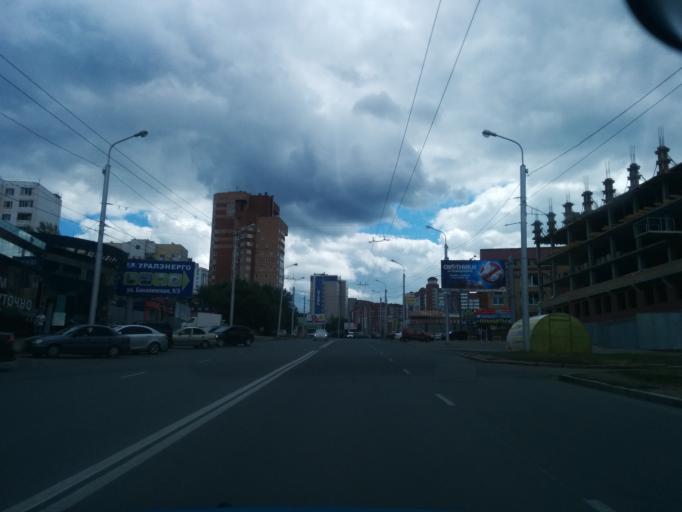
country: RU
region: Bashkortostan
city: Ufa
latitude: 54.7170
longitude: 55.9928
